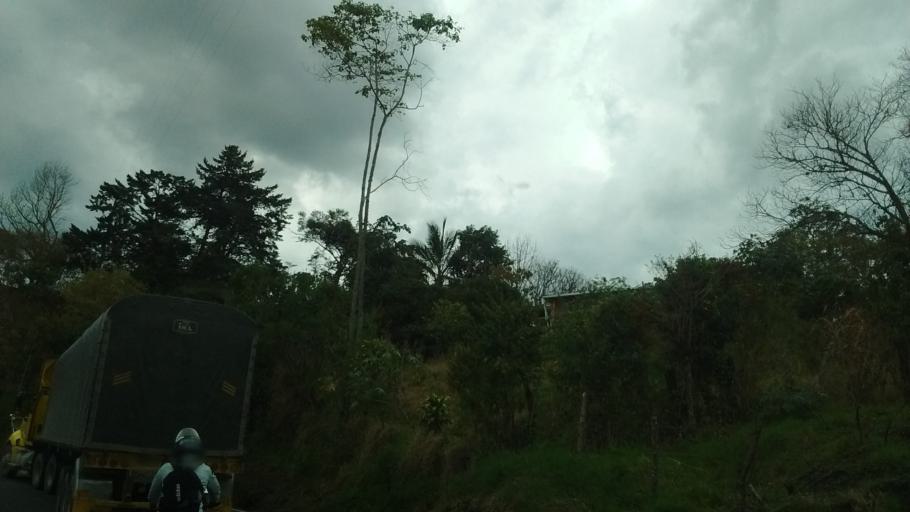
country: CO
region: Cauca
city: Rosas
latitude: 2.2749
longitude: -76.7190
